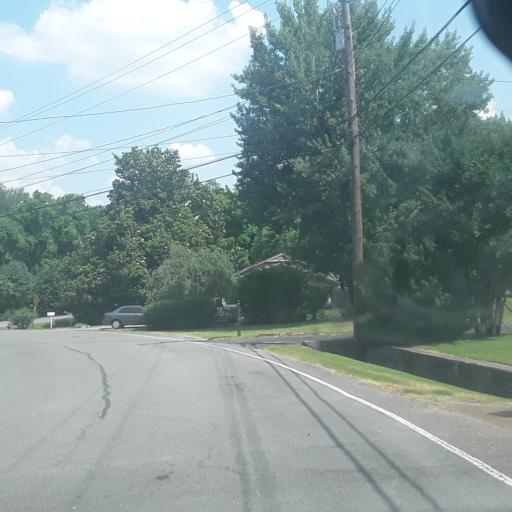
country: US
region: Tennessee
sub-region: Williamson County
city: Brentwood Estates
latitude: 36.0563
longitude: -86.7112
